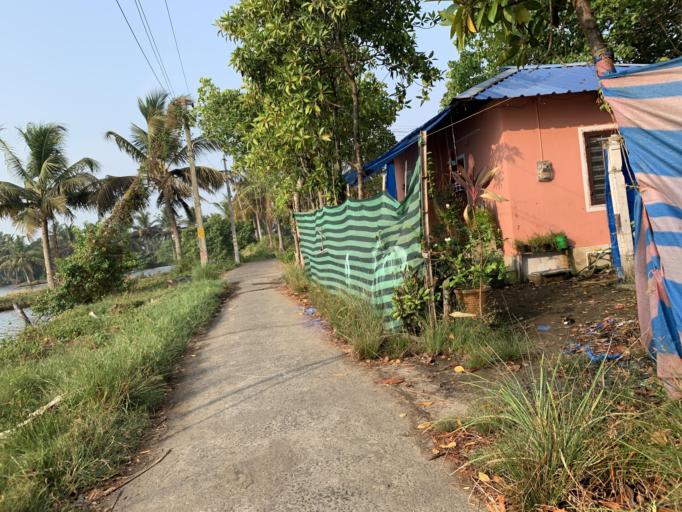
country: IN
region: Kerala
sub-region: Ernakulam
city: Elur
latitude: 10.0177
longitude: 76.2201
